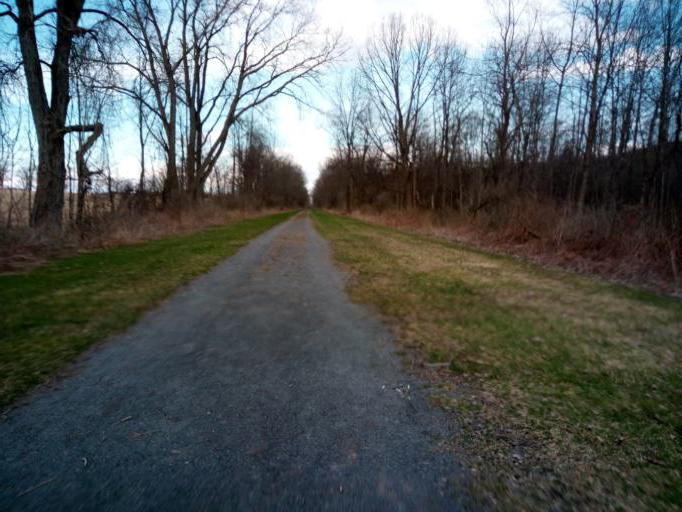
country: US
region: New York
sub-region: Chemung County
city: Big Flats
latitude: 42.1468
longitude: -76.9030
